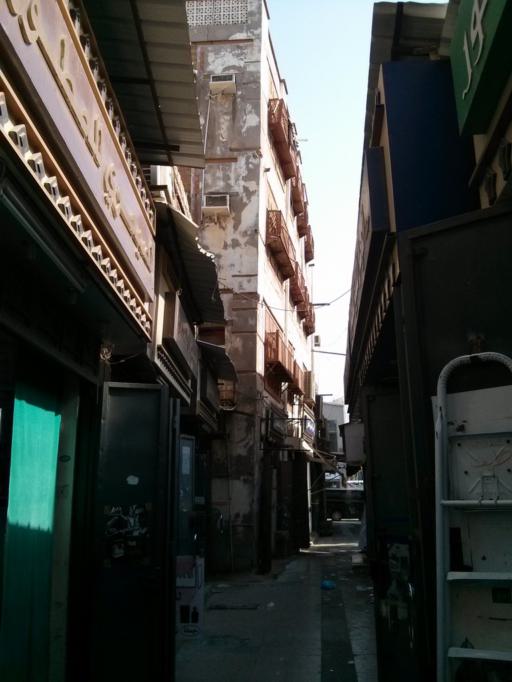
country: SA
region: Makkah
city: Jeddah
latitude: 21.4849
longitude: 39.1887
